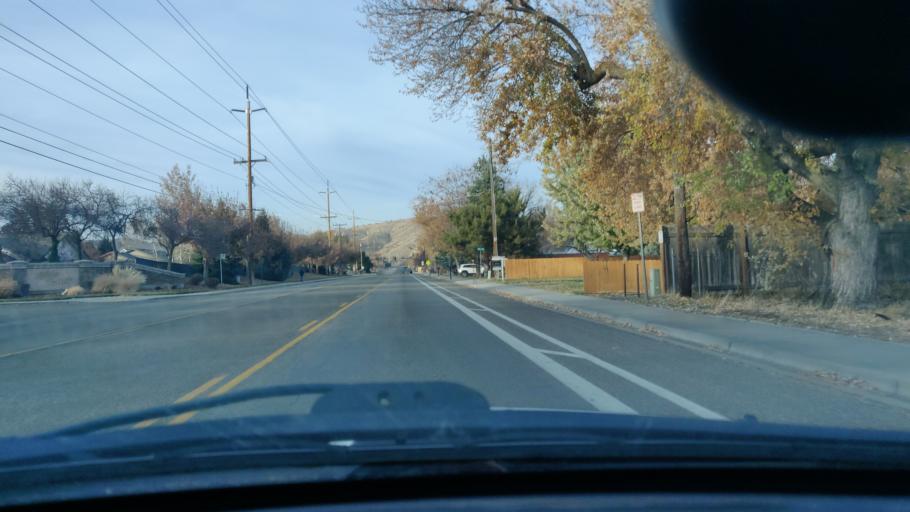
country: US
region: Idaho
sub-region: Ada County
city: Garden City
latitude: 43.6753
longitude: -116.2792
